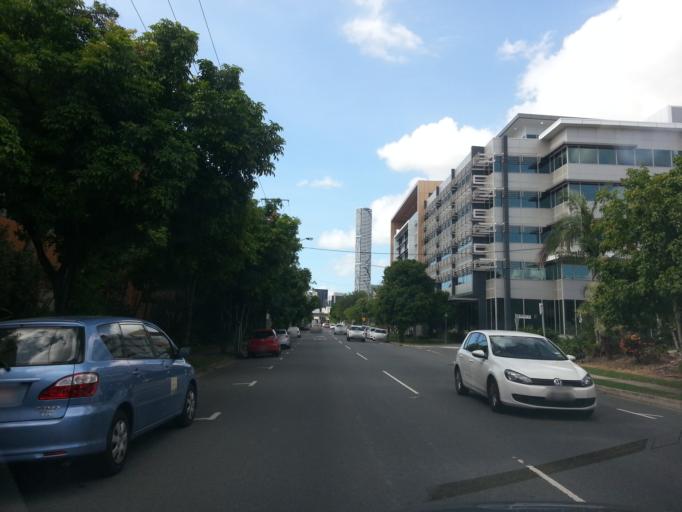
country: AU
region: Queensland
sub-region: Brisbane
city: Milton
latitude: -27.4750
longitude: 153.0102
